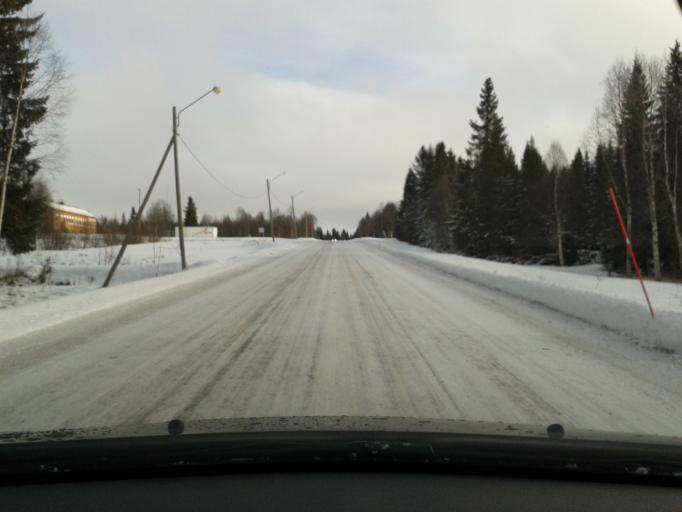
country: SE
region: Vaesterbotten
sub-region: Vilhelmina Kommun
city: Sjoberg
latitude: 64.7951
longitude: 16.0661
